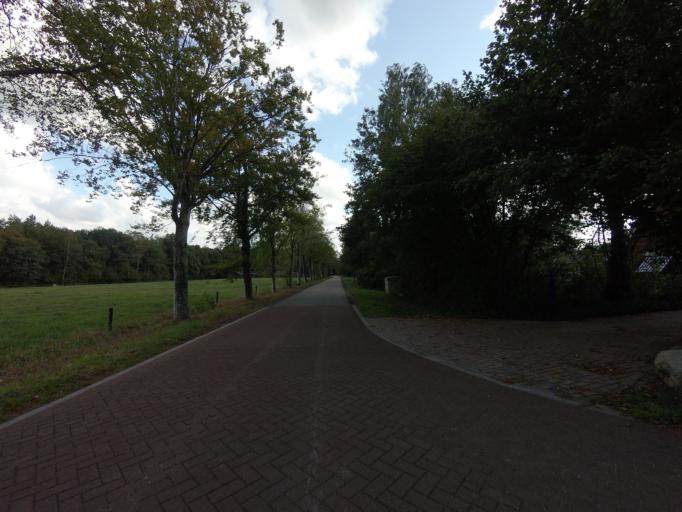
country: NL
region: Friesland
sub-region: Gemeente Heerenveen
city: Jubbega
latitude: 53.0062
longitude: 6.2323
